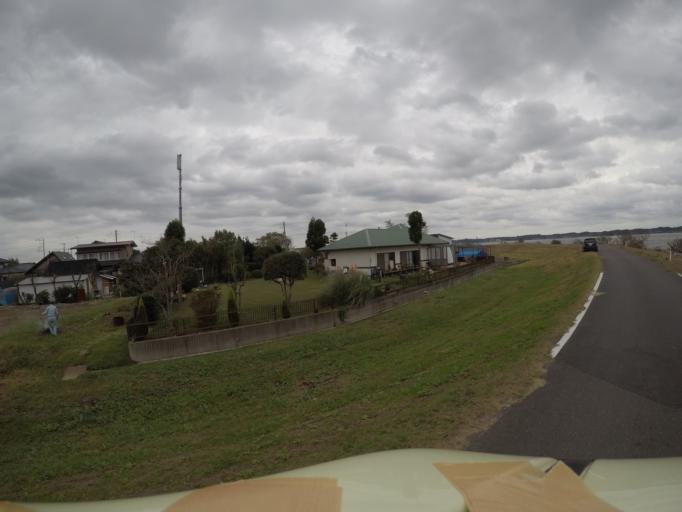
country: JP
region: Ibaraki
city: Ishioka
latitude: 36.1023
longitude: 140.3821
